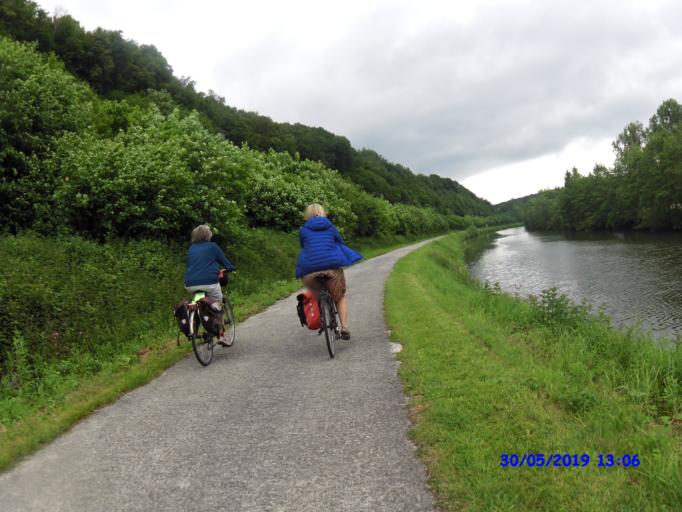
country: BE
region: Wallonia
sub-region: Province du Hainaut
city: Thuin
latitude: 50.3510
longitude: 4.3082
